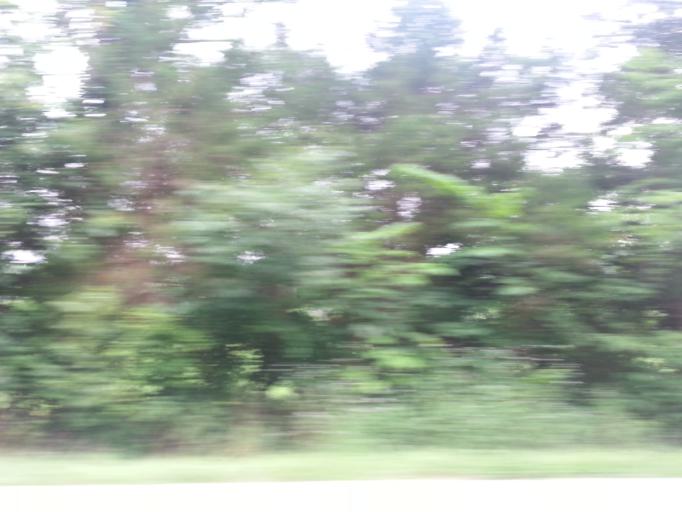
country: US
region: Kentucky
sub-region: Harrison County
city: Cynthiana
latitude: 38.5102
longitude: -84.2064
